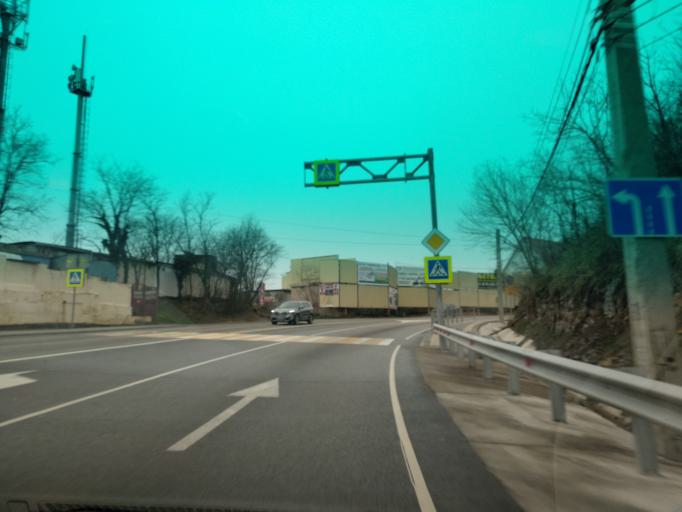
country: RU
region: Krasnodarskiy
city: Tuapse
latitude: 44.1054
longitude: 39.0765
